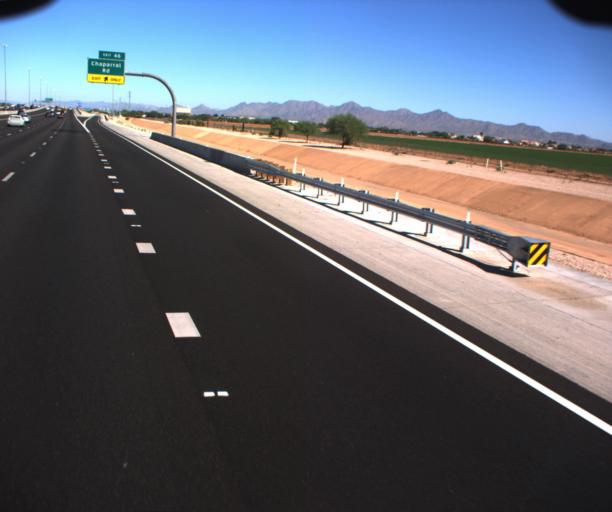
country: US
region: Arizona
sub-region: Maricopa County
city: Scottsdale
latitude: 33.5026
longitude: -111.8876
